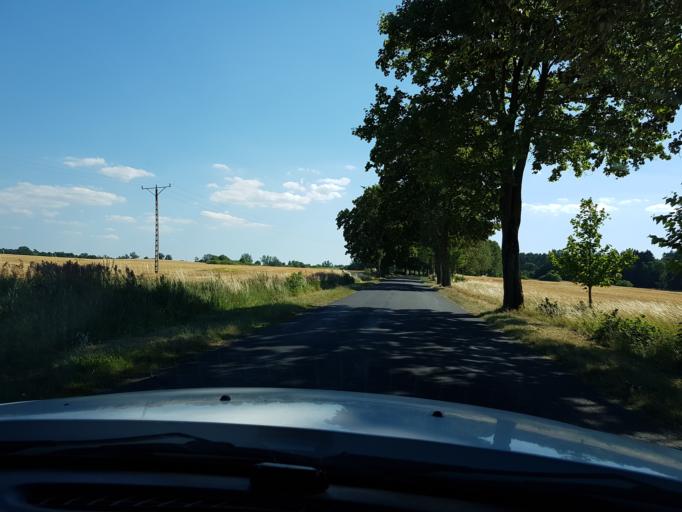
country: PL
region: West Pomeranian Voivodeship
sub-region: Powiat bialogardzki
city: Karlino
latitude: 53.9698
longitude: 15.9074
